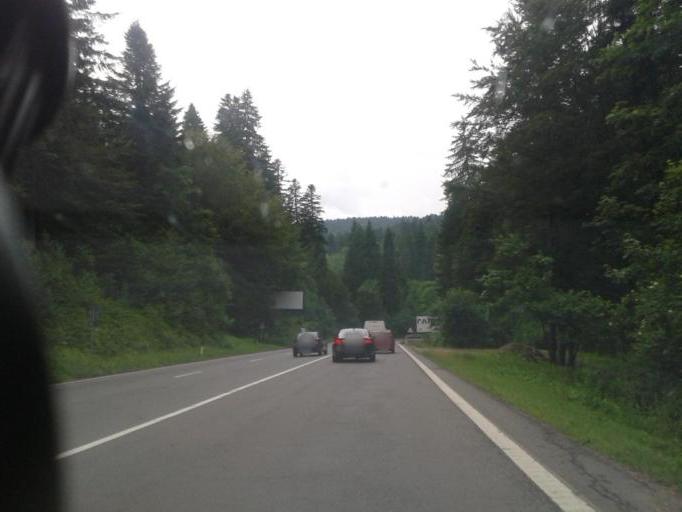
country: RO
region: Brasov
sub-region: Oras Predeal
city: Predeal
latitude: 45.5231
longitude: 25.5731
